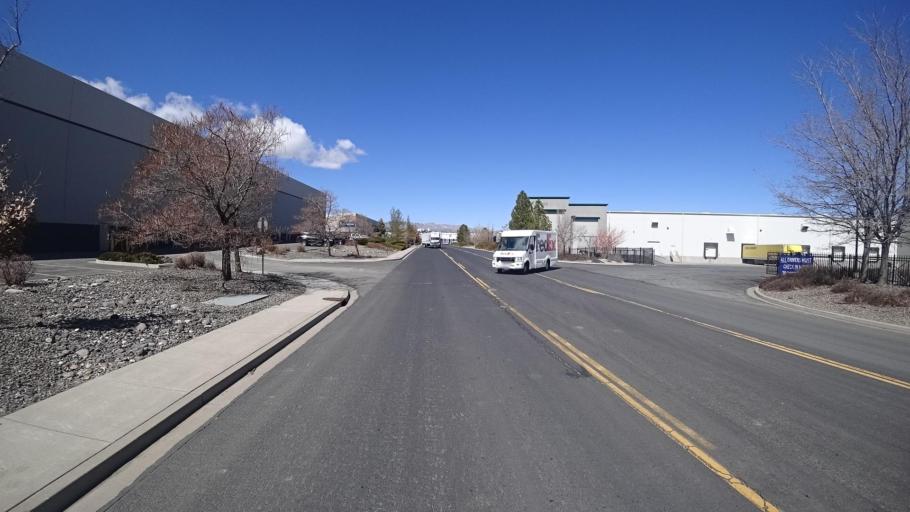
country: US
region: Nevada
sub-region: Washoe County
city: Lemmon Valley
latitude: 39.6460
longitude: -119.8613
